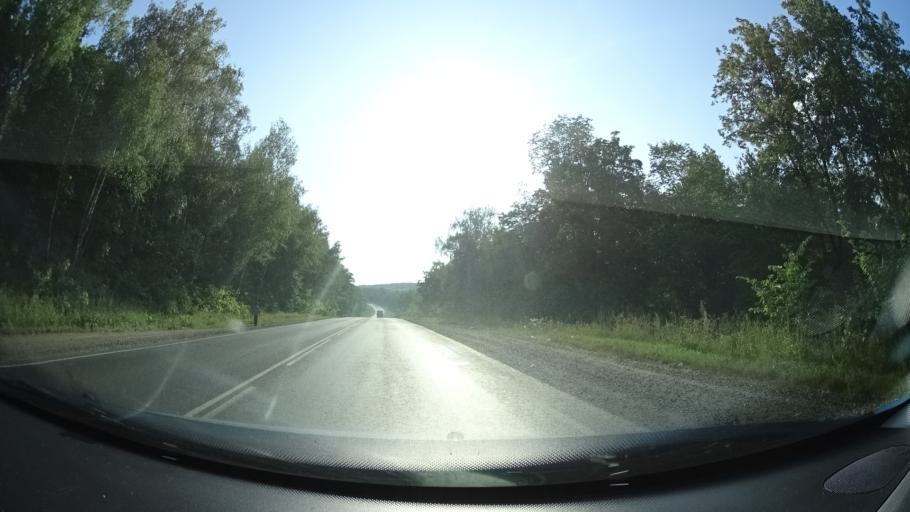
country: RU
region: Tatarstan
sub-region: Bavlinskiy Rayon
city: Bavly
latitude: 54.4569
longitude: 53.2728
